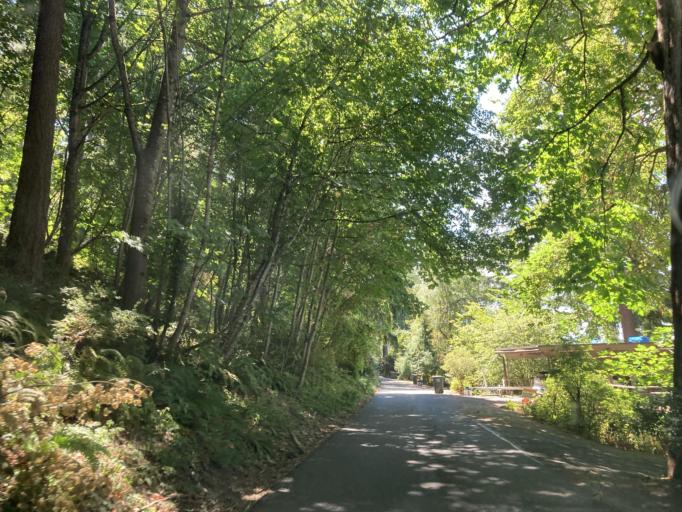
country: US
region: Washington
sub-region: Whatcom County
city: Bellingham
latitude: 48.7353
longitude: -122.4920
